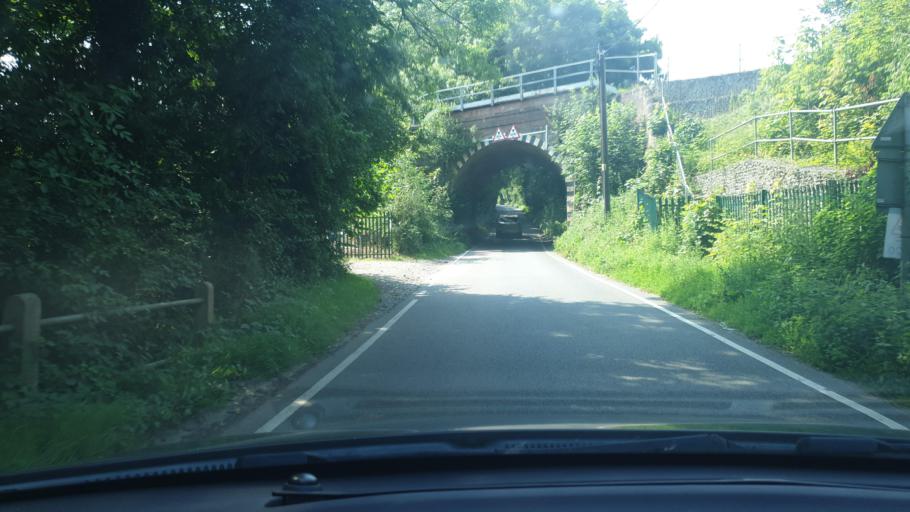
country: GB
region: England
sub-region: Suffolk
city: East Bergholt
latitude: 51.9459
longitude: 1.0223
